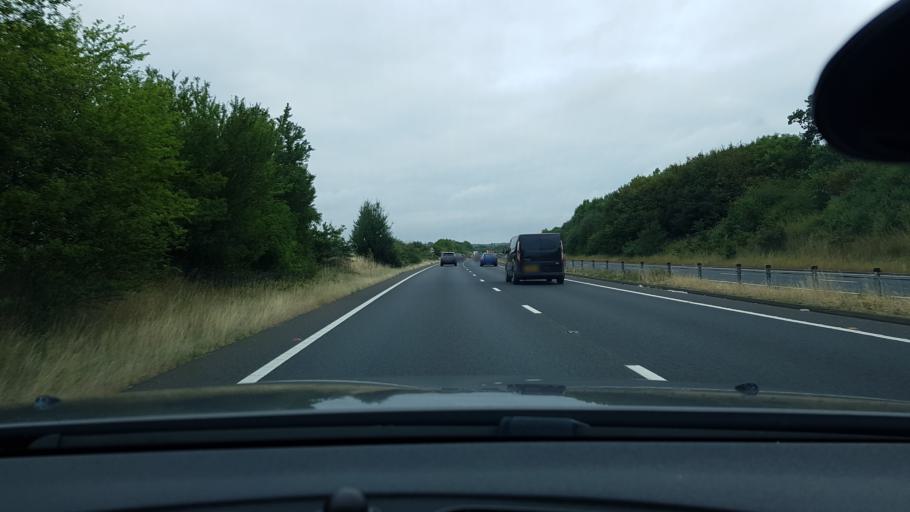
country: GB
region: England
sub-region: West Berkshire
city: Newbury
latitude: 51.3872
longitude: -1.3614
